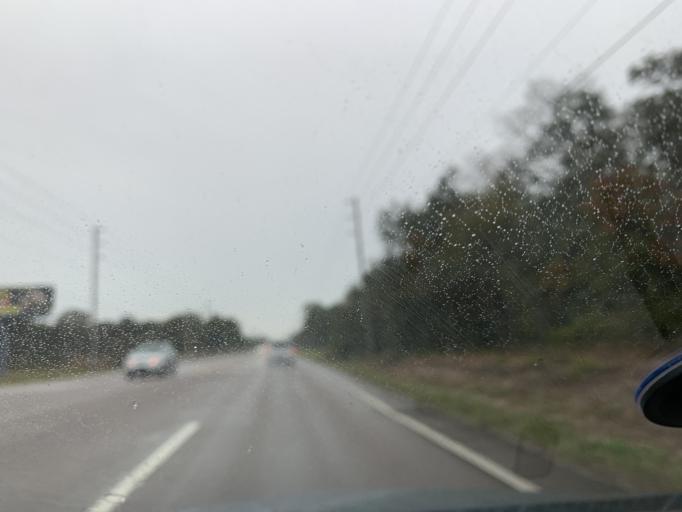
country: US
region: Florida
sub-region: Pasco County
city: Shady Hills
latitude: 28.4338
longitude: -82.5051
